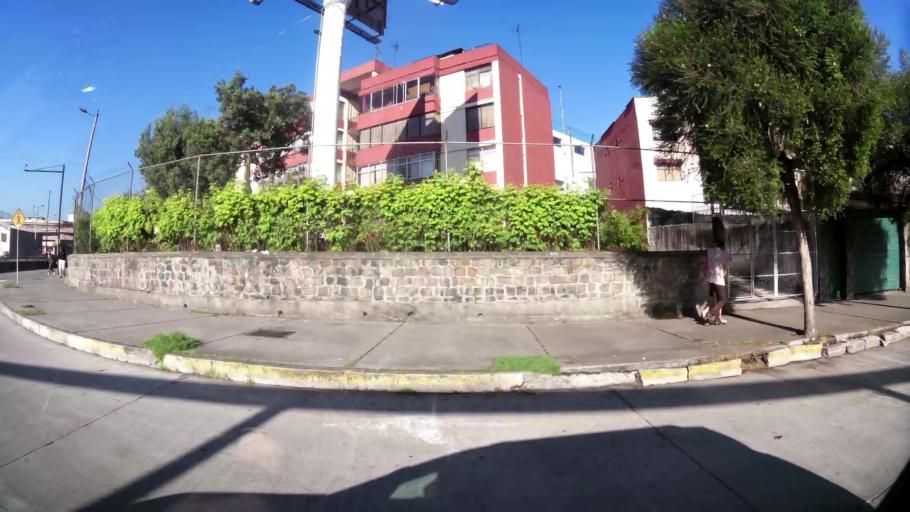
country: EC
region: Pichincha
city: Quito
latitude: -0.2447
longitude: -78.5193
